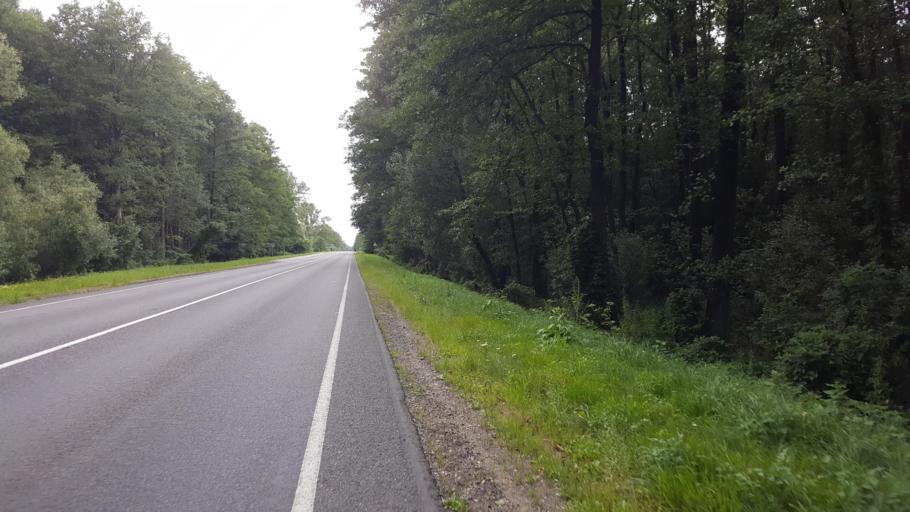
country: BY
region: Brest
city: Zhabinka
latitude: 52.2835
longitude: 23.9463
